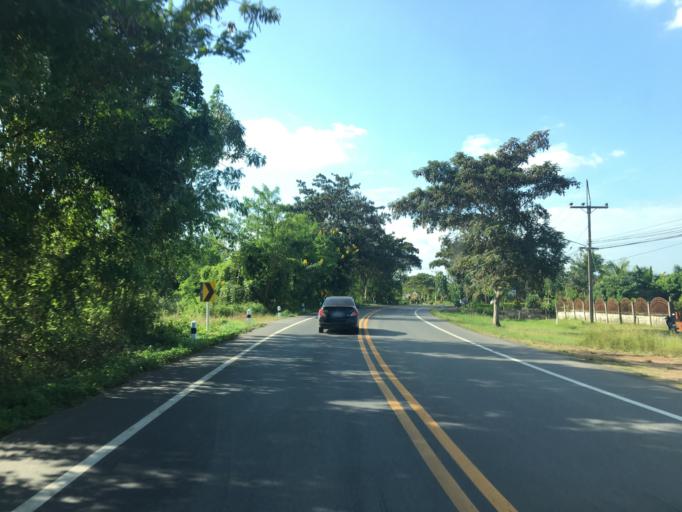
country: TH
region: Phayao
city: Chun
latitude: 19.3548
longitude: 100.0992
